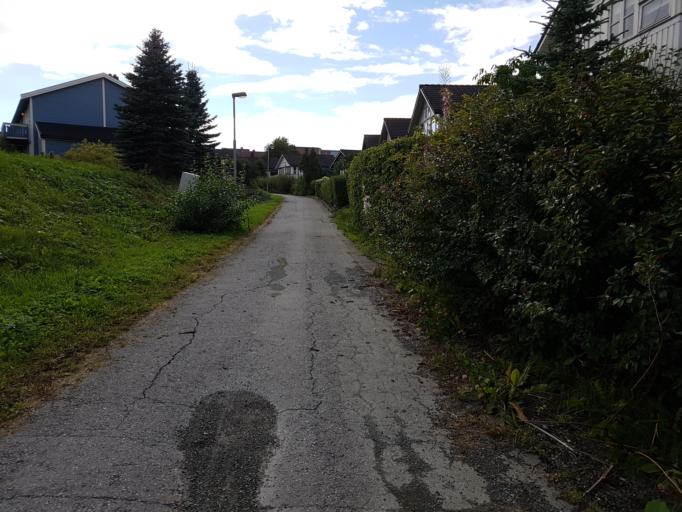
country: NO
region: Sor-Trondelag
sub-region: Trondheim
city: Trondheim
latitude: 63.4212
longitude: 10.4816
